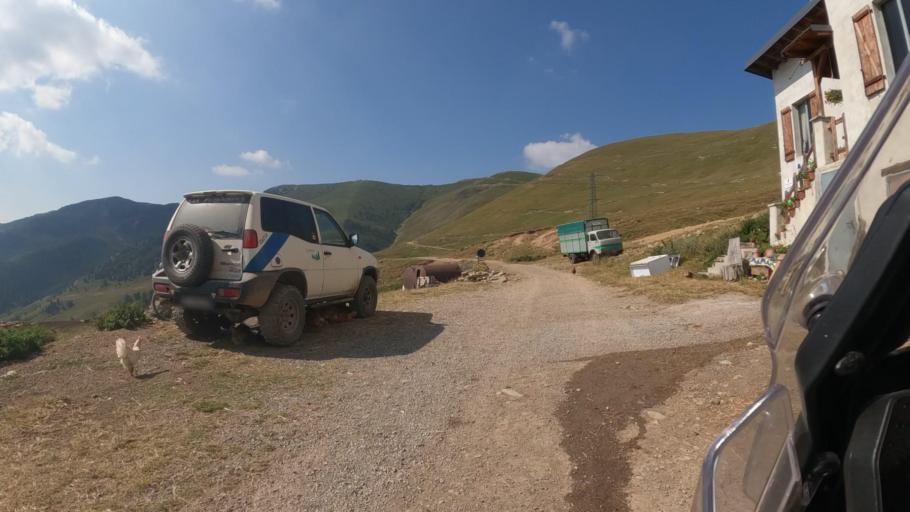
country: IT
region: Piedmont
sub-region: Provincia di Cuneo
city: Briga Alta
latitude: 44.0784
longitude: 7.7224
